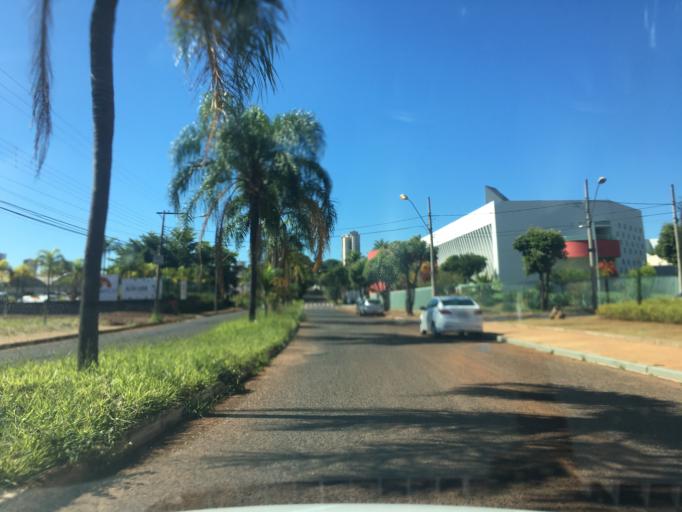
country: BR
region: Minas Gerais
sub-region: Uberlandia
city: Uberlandia
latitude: -18.9330
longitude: -48.2810
